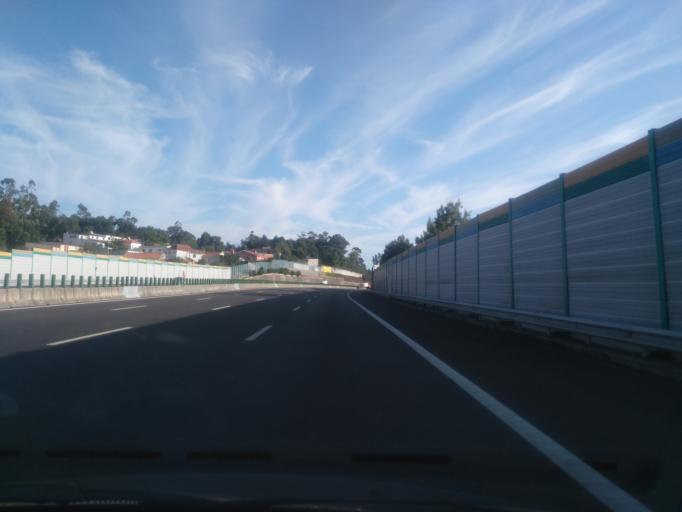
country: PT
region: Porto
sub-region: Vila Nova de Gaia
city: Grijo
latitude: 41.0323
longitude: -8.5723
